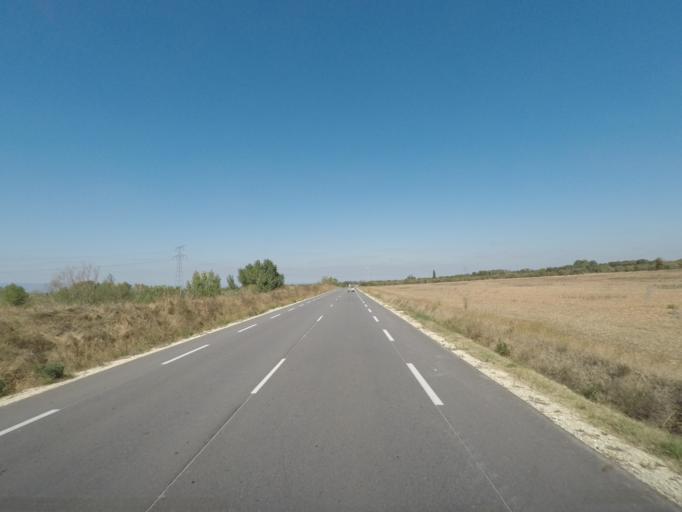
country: FR
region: Rhone-Alpes
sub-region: Departement de la Drome
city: Montmeyran
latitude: 44.8483
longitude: 5.0081
